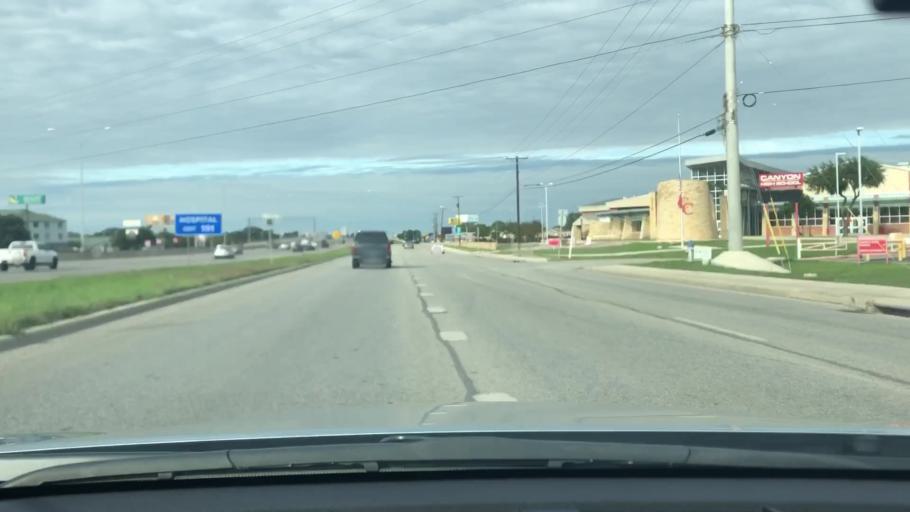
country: US
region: Texas
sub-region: Comal County
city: New Braunfels
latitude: 29.7082
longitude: -98.0896
